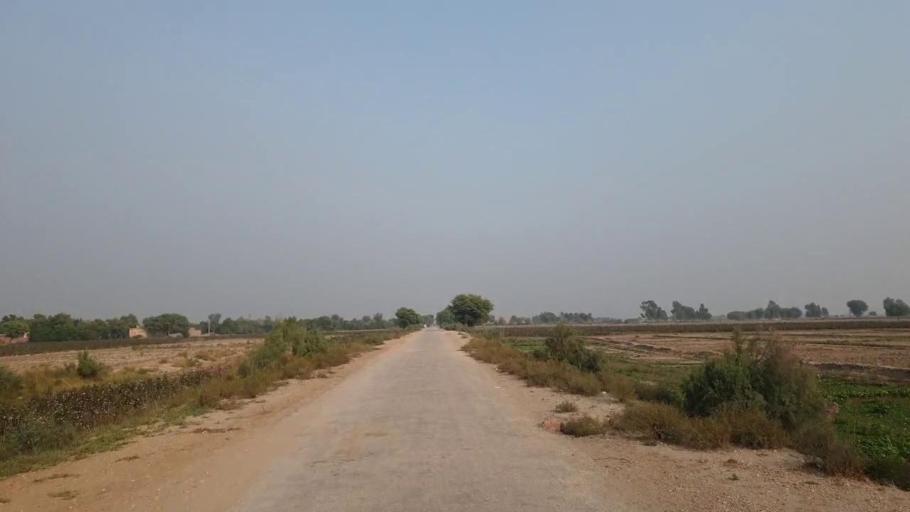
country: PK
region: Sindh
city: Bhan
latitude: 26.4951
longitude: 67.7248
